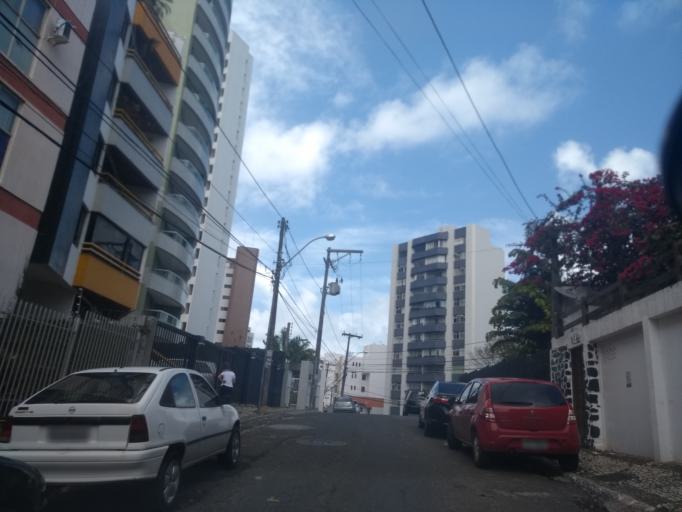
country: BR
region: Bahia
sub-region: Salvador
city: Salvador
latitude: -13.0033
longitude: -38.5163
